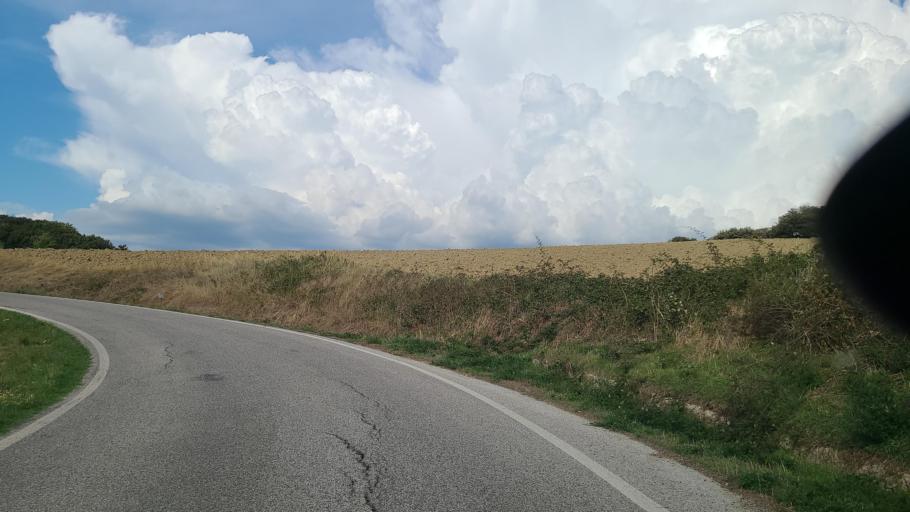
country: IT
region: Tuscany
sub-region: Provincia di Siena
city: San Gimignano
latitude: 43.4086
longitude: 10.9769
